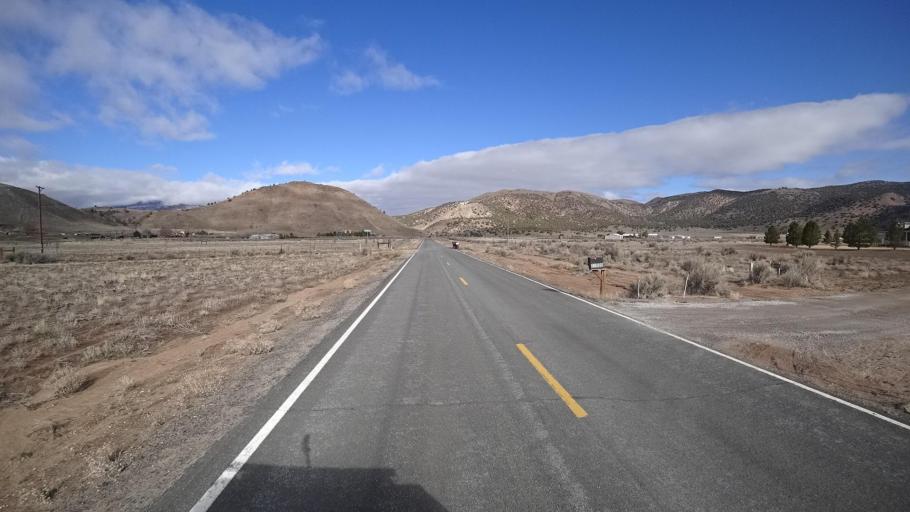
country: US
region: Nevada
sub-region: Washoe County
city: Cold Springs
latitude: 39.8947
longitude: -119.9804
